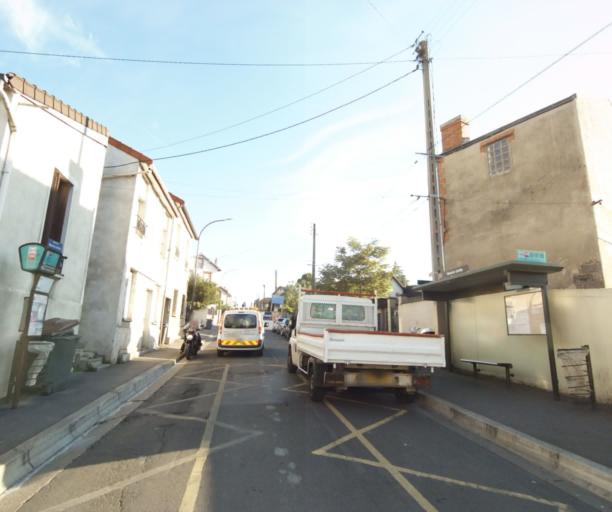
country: FR
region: Ile-de-France
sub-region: Departement du Val-d'Oise
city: Argenteuil
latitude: 48.9401
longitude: 2.2345
